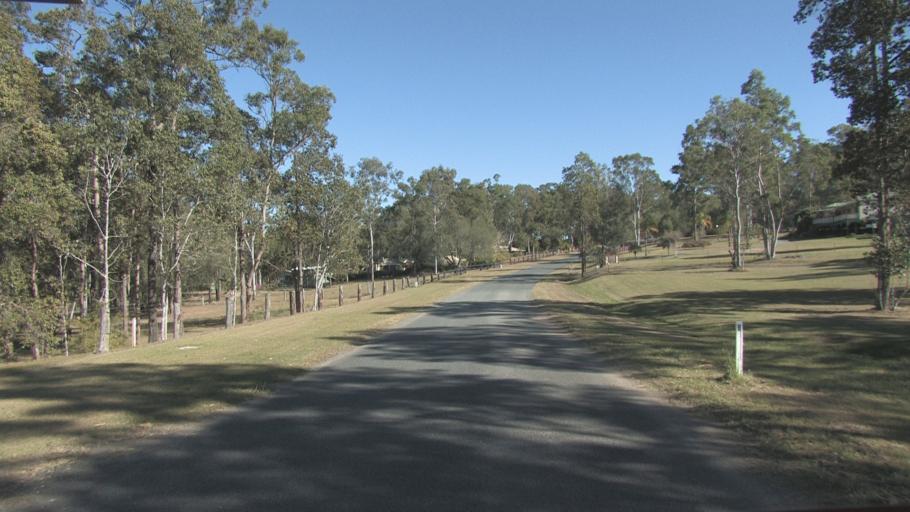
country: AU
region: Queensland
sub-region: Logan
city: North Maclean
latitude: -27.8321
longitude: 152.9370
